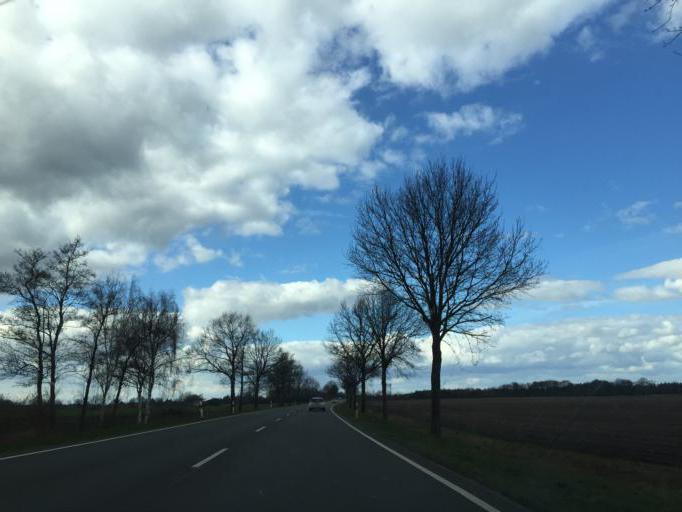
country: DE
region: Lower Saxony
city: Broeckel
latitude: 52.5002
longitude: 10.2333
